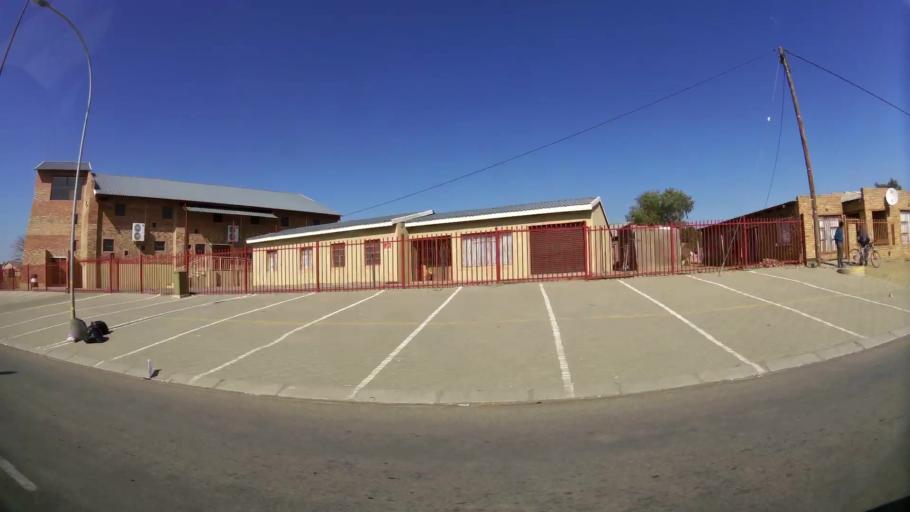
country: ZA
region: Orange Free State
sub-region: Mangaung Metropolitan Municipality
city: Bloemfontein
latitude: -29.1569
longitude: 26.2449
